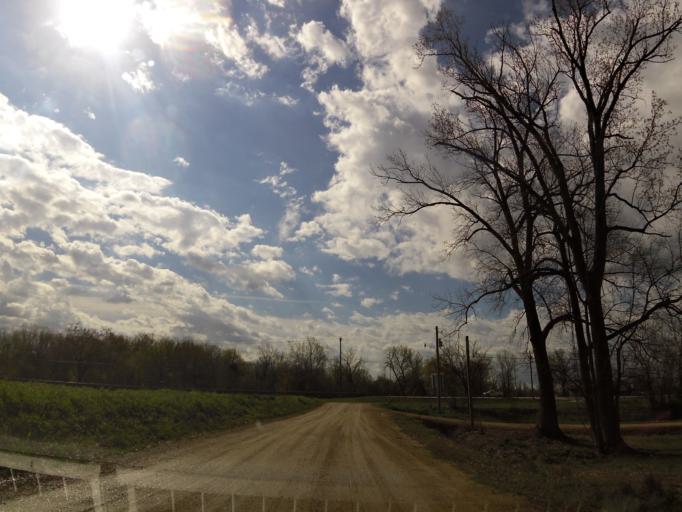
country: US
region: Missouri
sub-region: Butler County
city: Poplar Bluff
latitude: 36.7631
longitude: -90.3793
